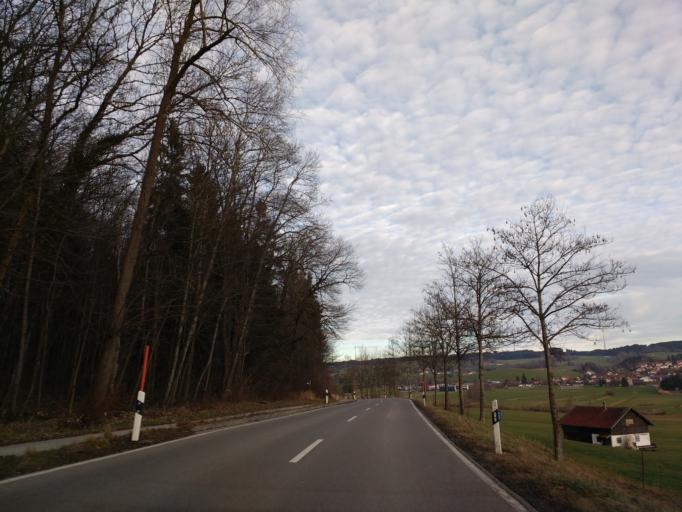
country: DE
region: Bavaria
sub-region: Swabia
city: Wildpoldsried
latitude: 47.7663
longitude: 10.3845
